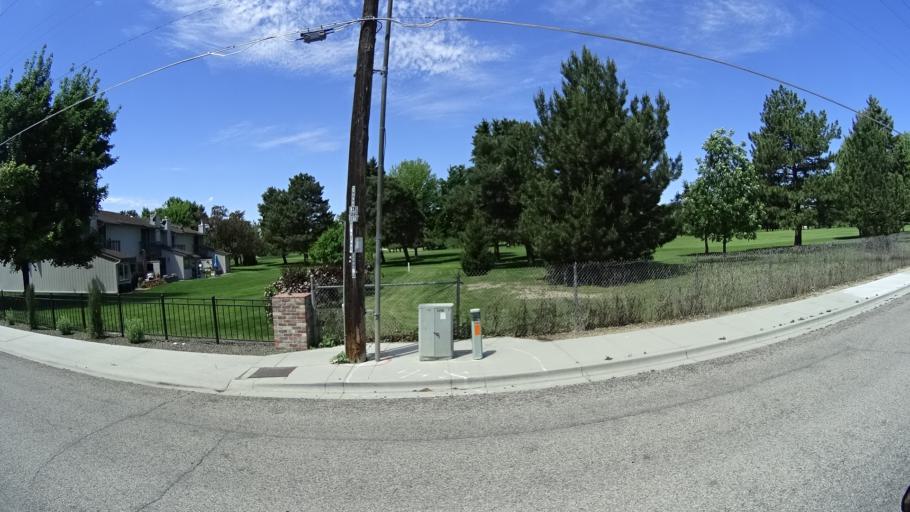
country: US
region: Idaho
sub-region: Ada County
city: Garden City
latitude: 43.5766
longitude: -116.2335
